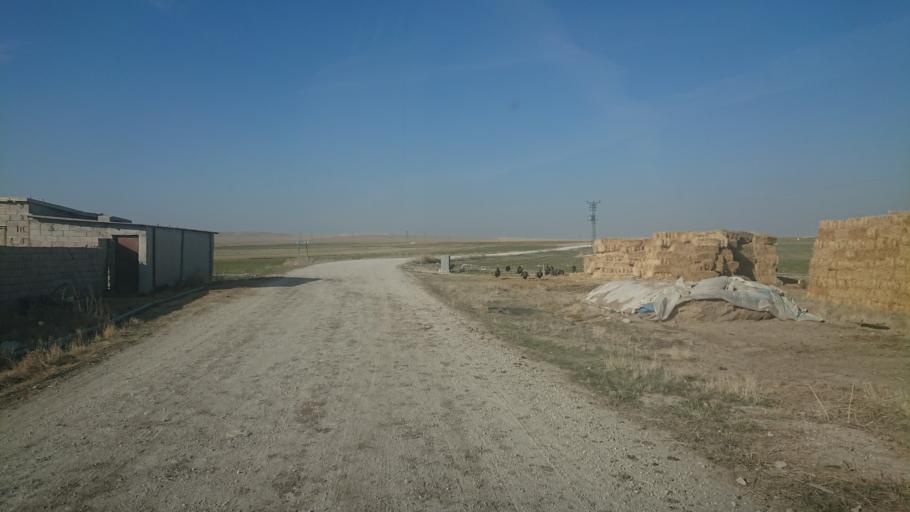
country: TR
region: Aksaray
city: Sultanhani
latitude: 38.0392
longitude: 33.6064
